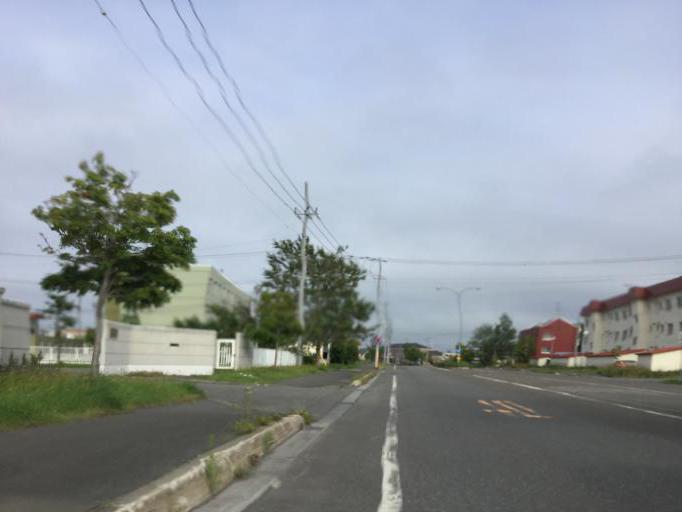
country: JP
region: Hokkaido
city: Wakkanai
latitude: 45.3947
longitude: 141.6933
